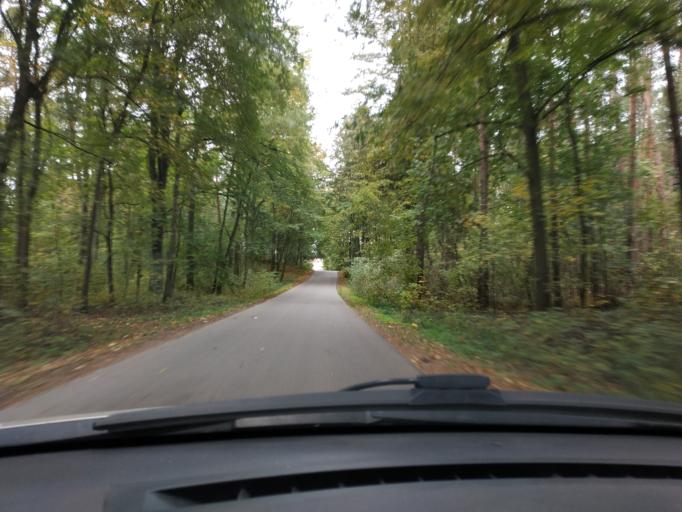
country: PL
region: Warmian-Masurian Voivodeship
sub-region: Powiat nowomiejski
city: Biskupiec
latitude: 53.4500
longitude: 19.3043
